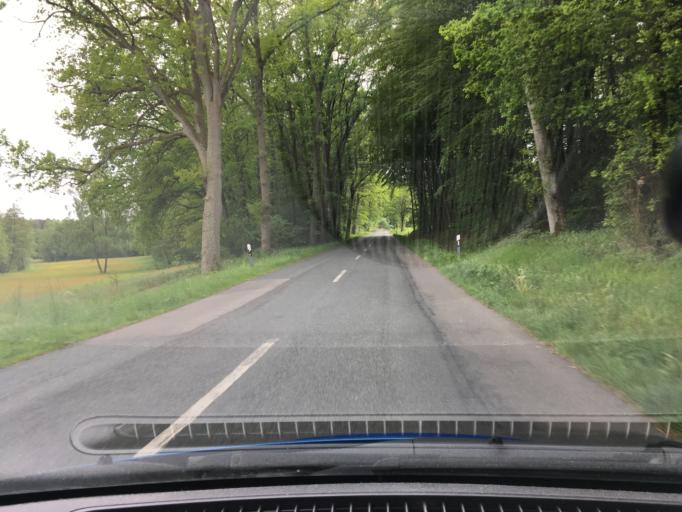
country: DE
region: Lower Saxony
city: Rehlingen
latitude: 53.0991
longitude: 10.2131
